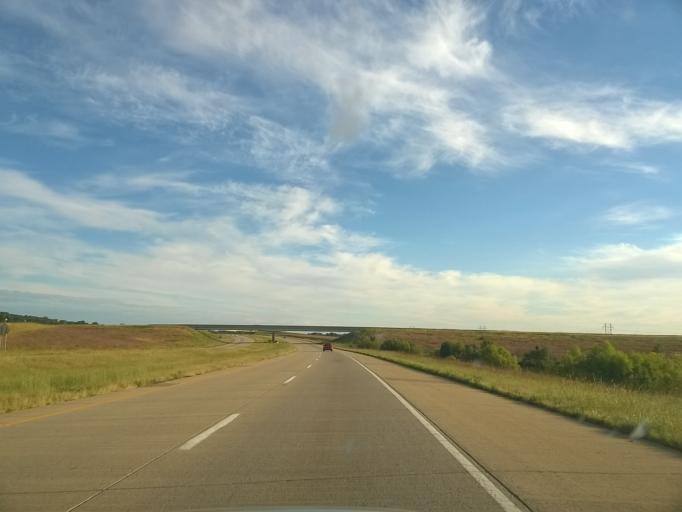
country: US
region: Indiana
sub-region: Vanderburgh County
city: Darmstadt
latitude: 38.1333
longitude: -87.4733
